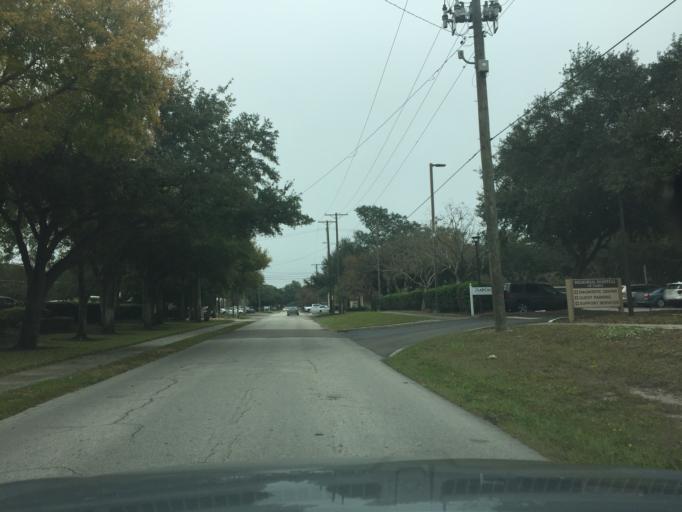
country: US
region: Florida
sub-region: Hillsborough County
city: Tampa
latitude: 27.9386
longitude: -82.4881
